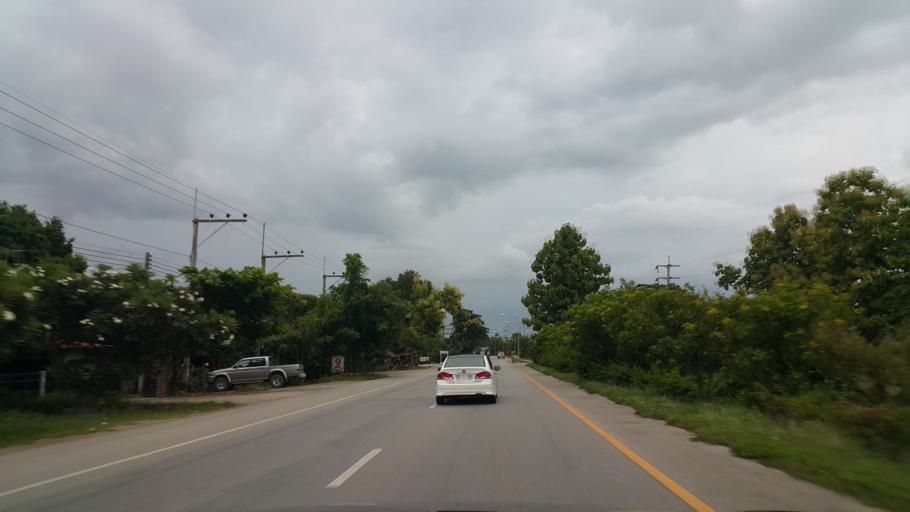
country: TH
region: Phayao
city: Phayao
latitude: 19.1257
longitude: 99.9090
